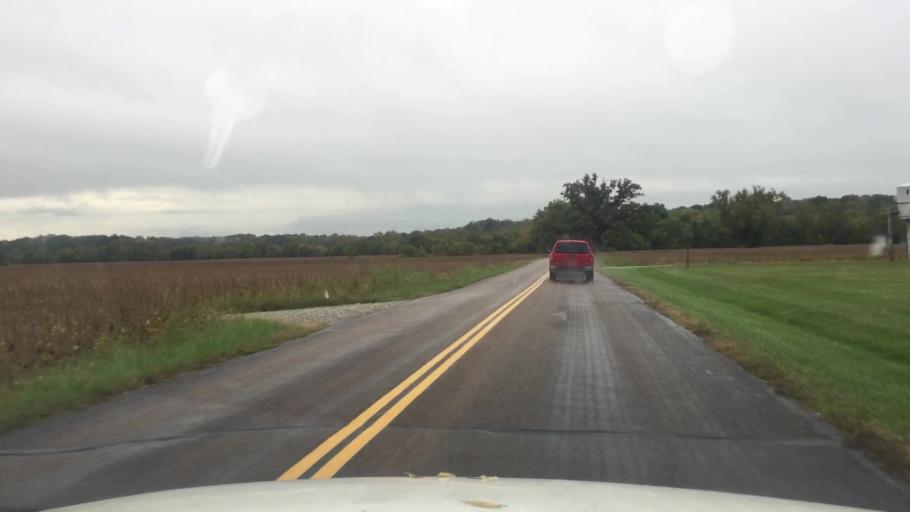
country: US
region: Missouri
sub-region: Boone County
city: Columbia
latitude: 38.8965
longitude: -92.4646
